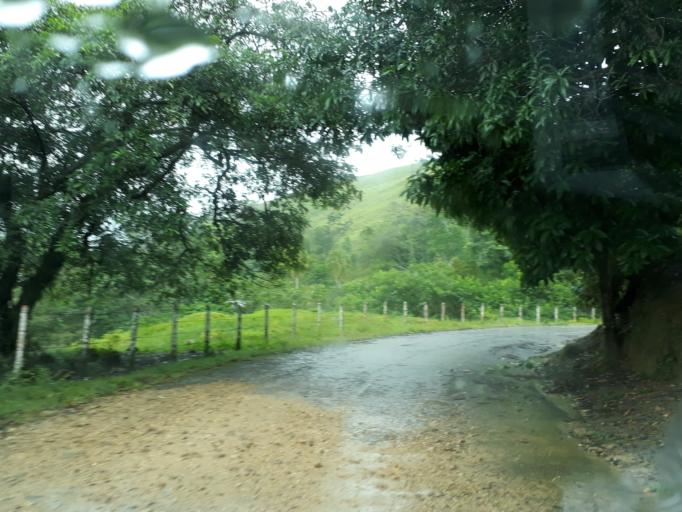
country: CO
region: Boyaca
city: Santa Maria
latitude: 4.7075
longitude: -73.3005
